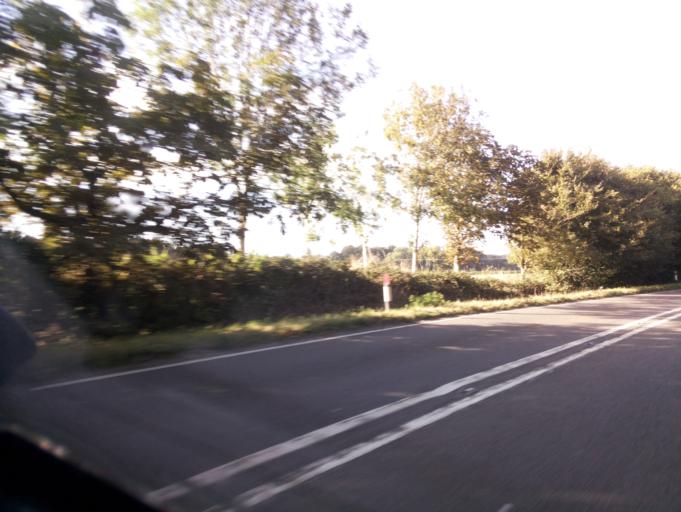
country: GB
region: England
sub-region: Hampshire
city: Alton
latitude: 51.1166
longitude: -0.9959
